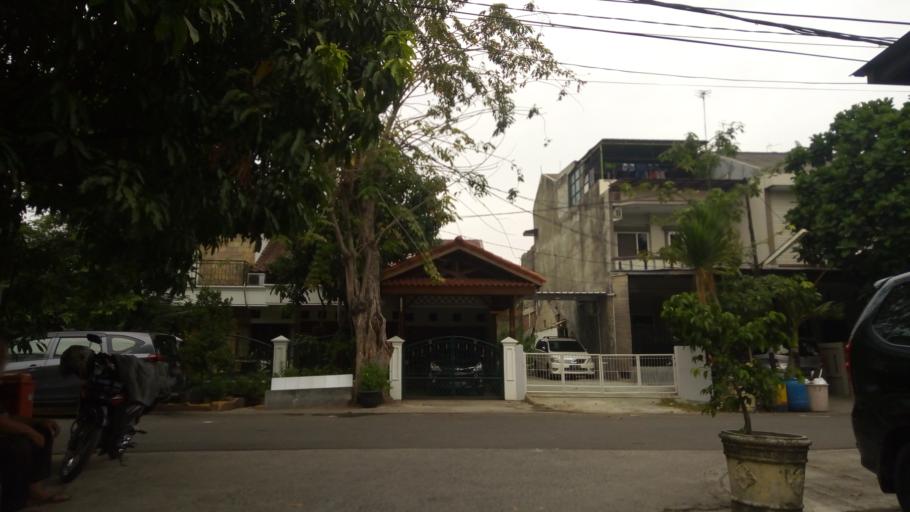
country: ID
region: Jakarta Raya
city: Jakarta
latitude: -6.1492
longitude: 106.8403
